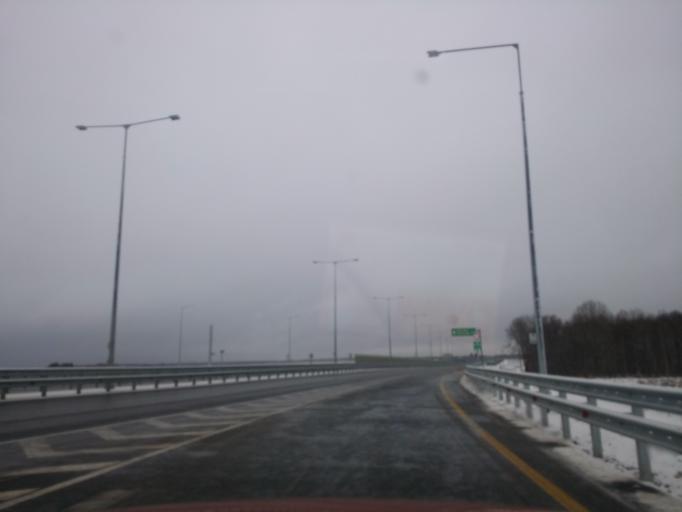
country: RU
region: Tverskaya
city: Likhoslavl'
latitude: 56.9810
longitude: 35.4244
